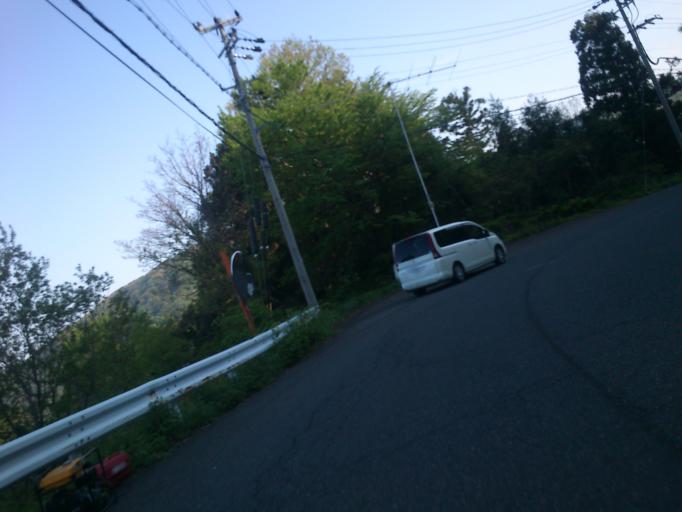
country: JP
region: Kyoto
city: Miyazu
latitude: 35.7121
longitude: 135.1936
